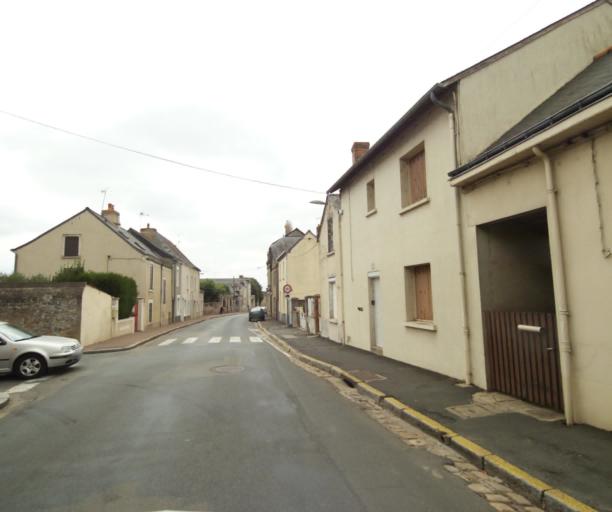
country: FR
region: Pays de la Loire
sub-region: Departement de la Sarthe
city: Sable-sur-Sarthe
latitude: 47.8359
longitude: -0.3232
